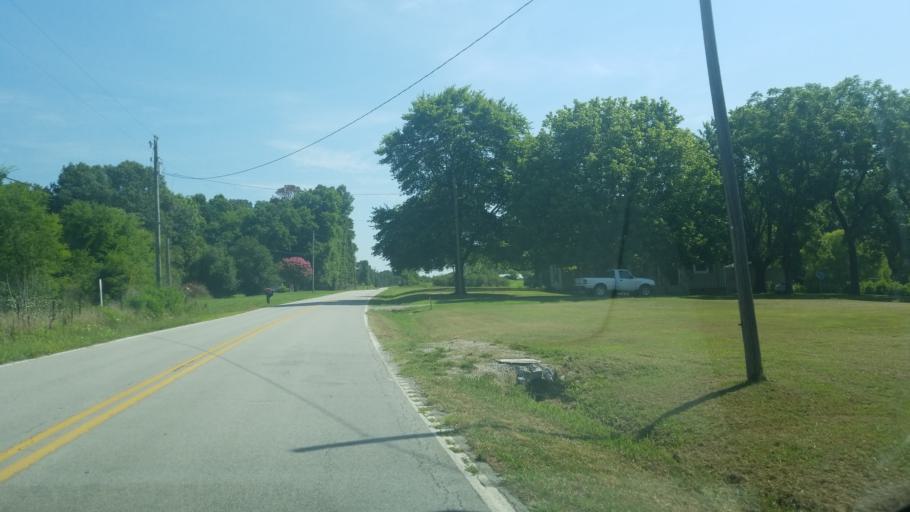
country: US
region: Tennessee
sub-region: Hamilton County
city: Sale Creek
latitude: 35.3445
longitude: -85.0022
